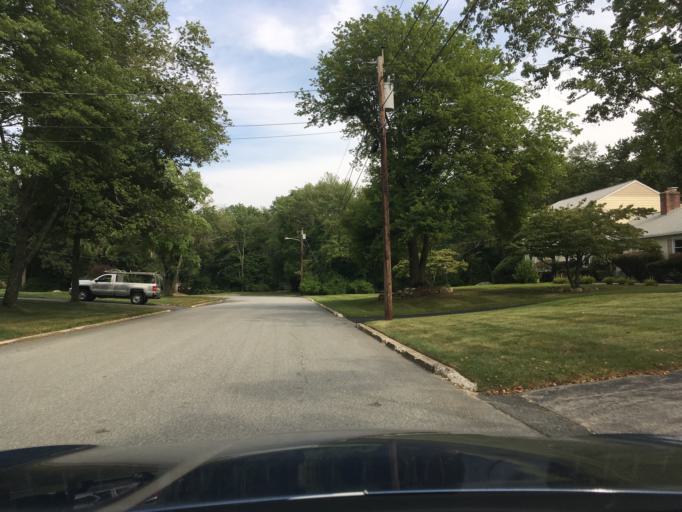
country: US
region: Rhode Island
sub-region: Kent County
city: East Greenwich
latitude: 41.6531
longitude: -71.4713
